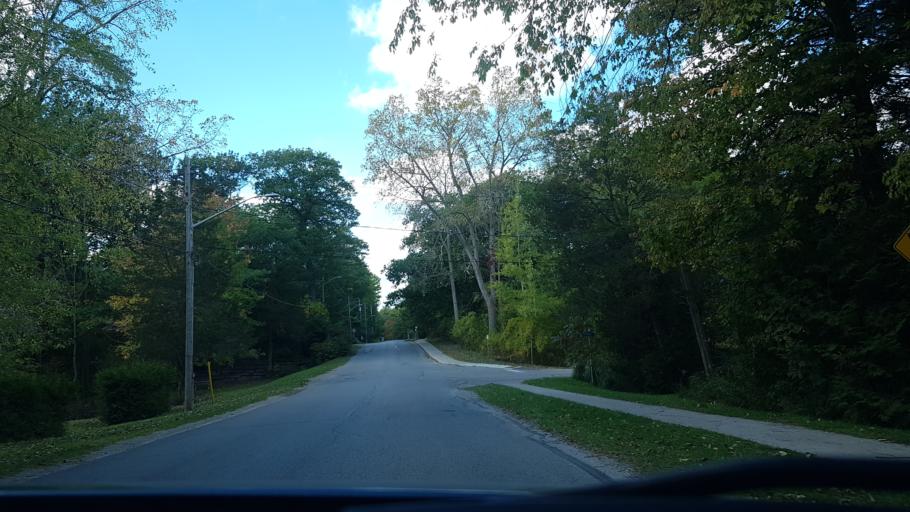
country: CA
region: Ontario
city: Lambton Shores
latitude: 43.3101
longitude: -81.7619
